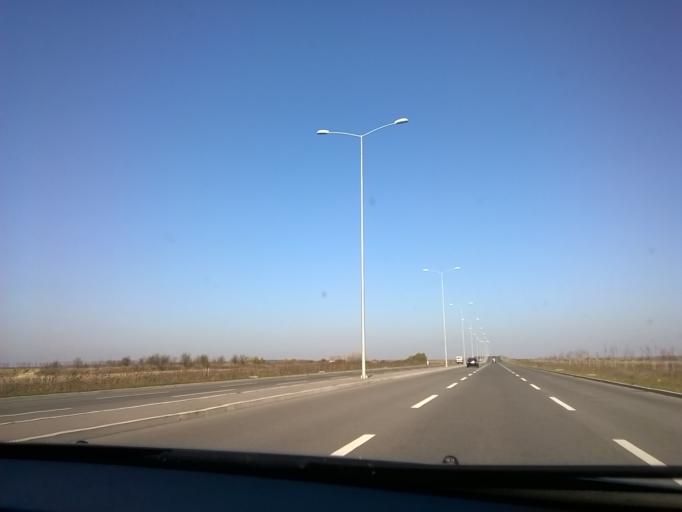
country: RS
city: Ovca
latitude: 44.9021
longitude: 20.5139
